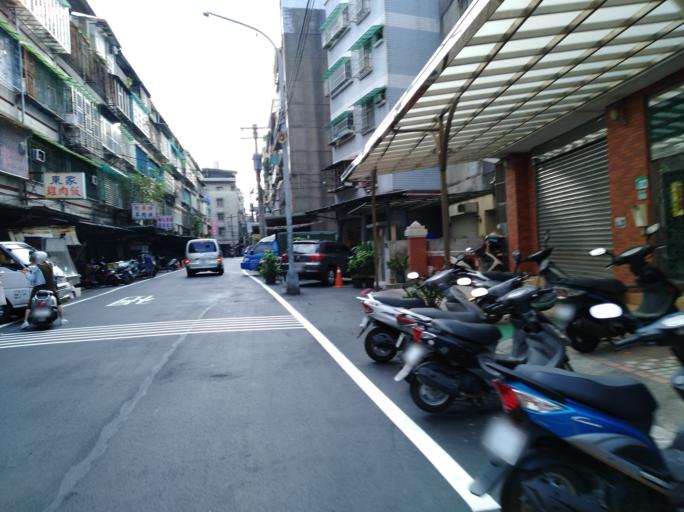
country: TW
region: Taipei
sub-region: Taipei
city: Banqiao
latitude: 25.0409
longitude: 121.4257
